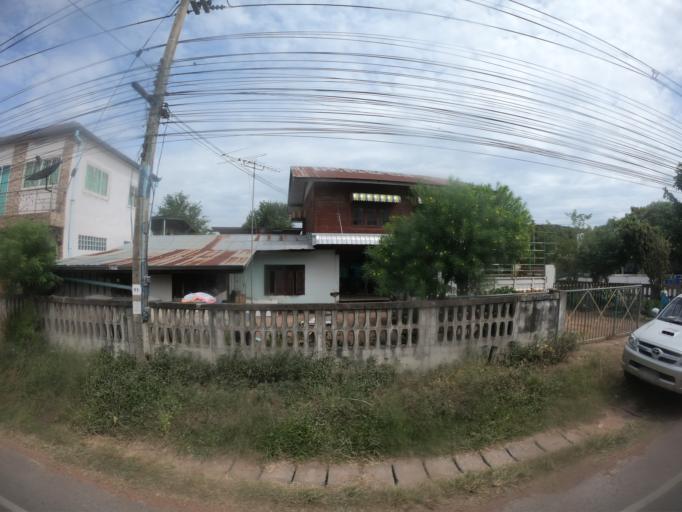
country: TH
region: Maha Sarakham
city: Chiang Yuen
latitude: 16.3478
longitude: 103.1220
